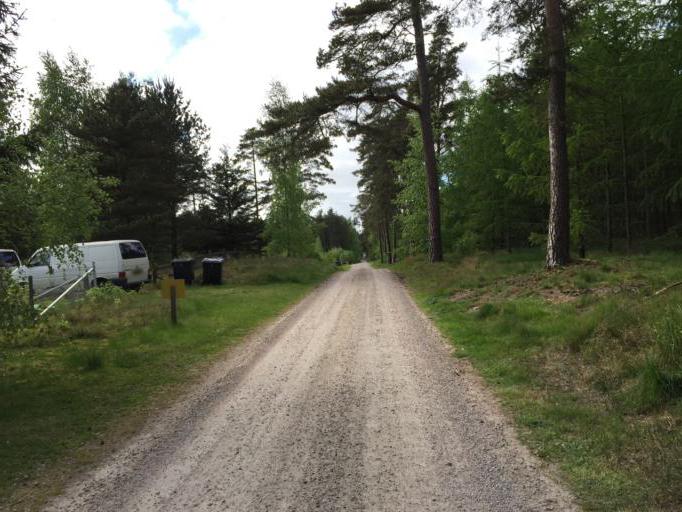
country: SE
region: Skane
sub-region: Sjobo Kommun
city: Sjoebo
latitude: 55.6655
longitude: 13.6360
